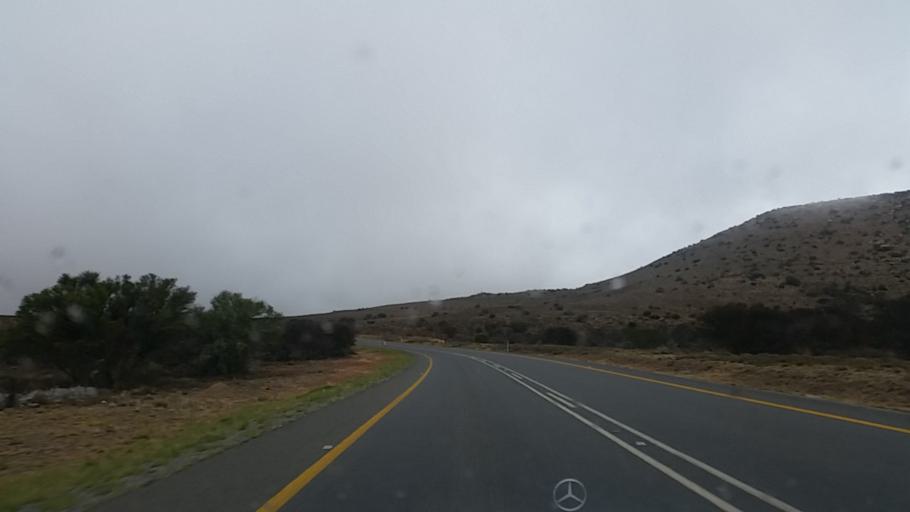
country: ZA
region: Eastern Cape
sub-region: Cacadu District Municipality
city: Graaff-Reinet
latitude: -31.9451
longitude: 24.7279
